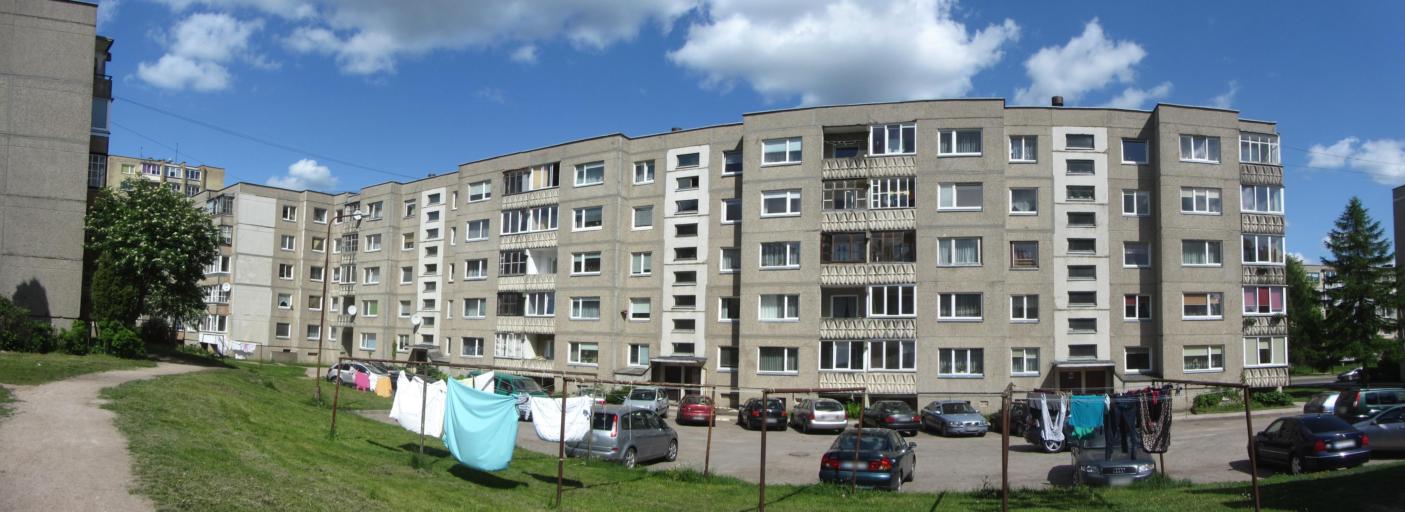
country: LT
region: Utenos apskritis
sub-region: Utena
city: Utena
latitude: 55.5089
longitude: 25.5835
